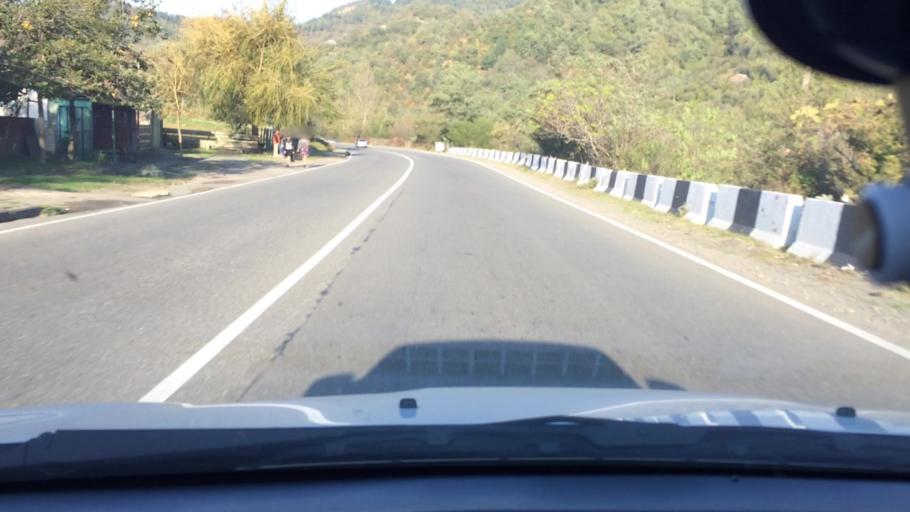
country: GE
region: Imereti
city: Kharagauli
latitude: 42.1090
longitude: 43.3337
